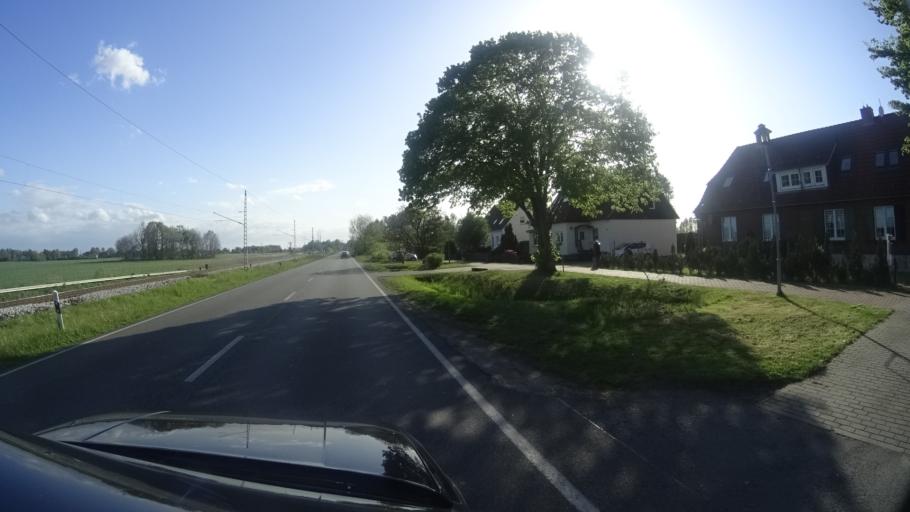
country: DE
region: Mecklenburg-Vorpommern
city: Rovershagen
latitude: 54.1800
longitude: 12.2565
